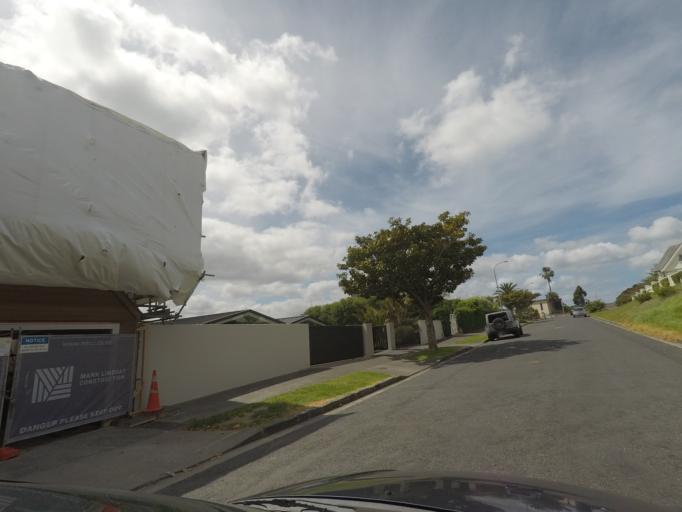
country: NZ
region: Auckland
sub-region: Auckland
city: Auckland
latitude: -36.8455
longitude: 174.7257
